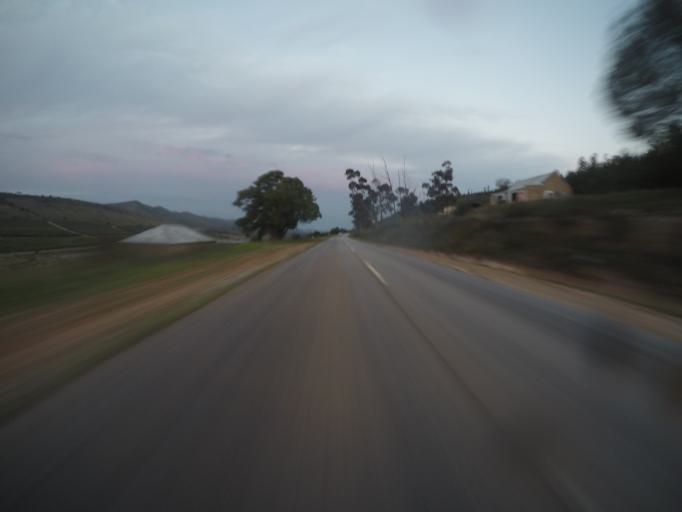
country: ZA
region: Western Cape
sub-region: Eden District Municipality
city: Plettenberg Bay
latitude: -33.8049
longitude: 23.6740
